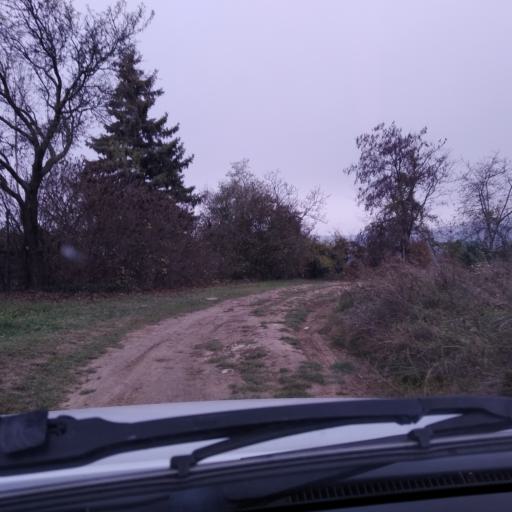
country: HU
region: Pest
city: Pomaz
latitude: 47.6384
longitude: 19.0187
